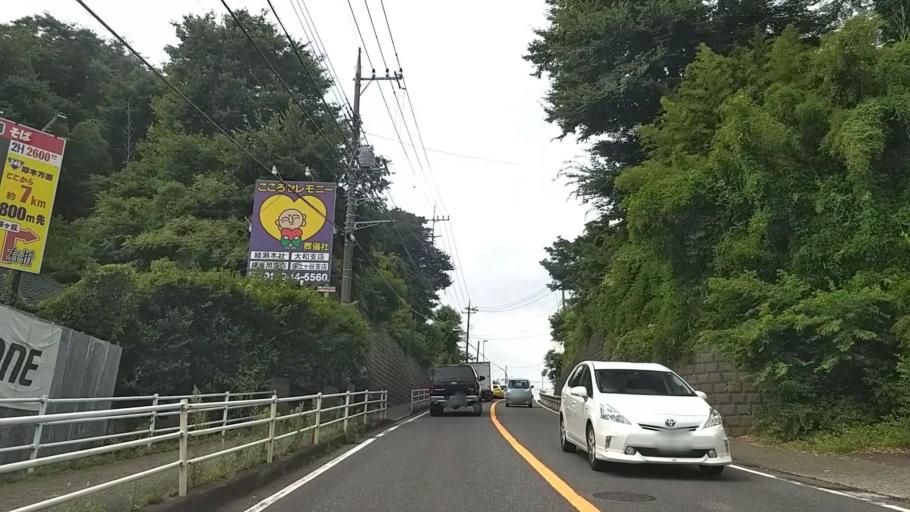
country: JP
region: Kanagawa
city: Minami-rinkan
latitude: 35.4540
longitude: 139.4748
